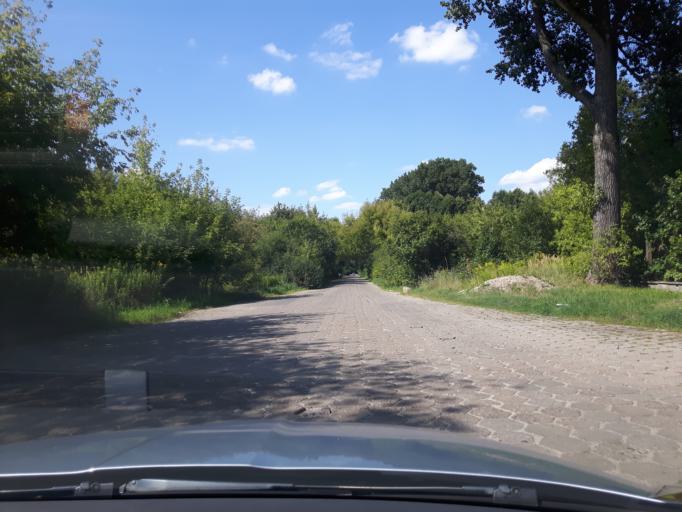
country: PL
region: Masovian Voivodeship
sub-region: Powiat wolominski
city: Zabki
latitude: 52.2715
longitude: 21.0935
